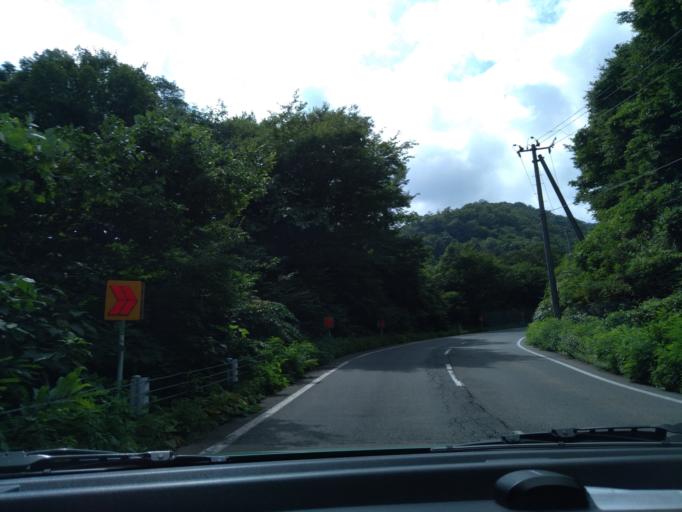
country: JP
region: Iwate
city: Morioka-shi
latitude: 39.6306
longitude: 141.0788
